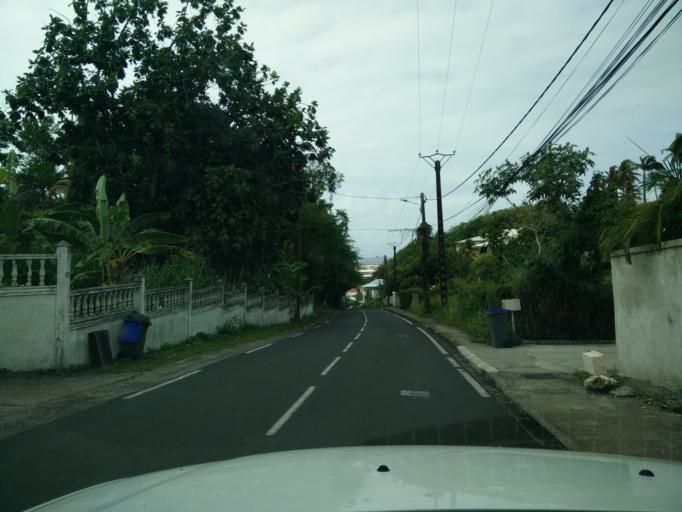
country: GP
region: Guadeloupe
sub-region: Guadeloupe
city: Le Gosier
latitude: 16.2132
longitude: -61.4660
